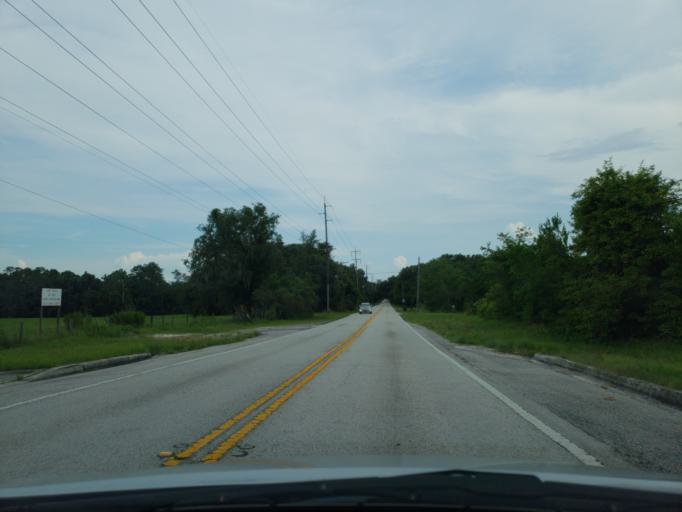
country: US
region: Florida
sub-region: Hillsborough County
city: University
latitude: 28.1061
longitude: -82.4308
